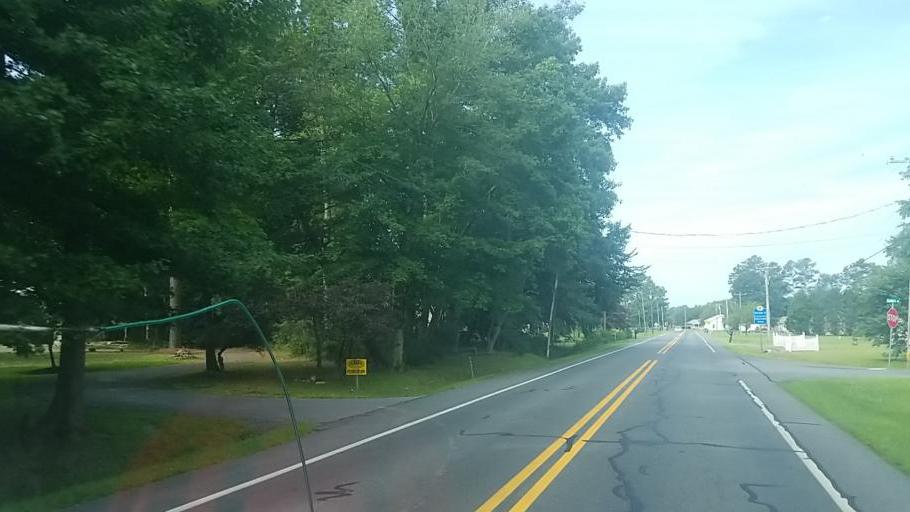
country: US
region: Delaware
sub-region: Sussex County
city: Selbyville
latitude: 38.5258
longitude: -75.2156
